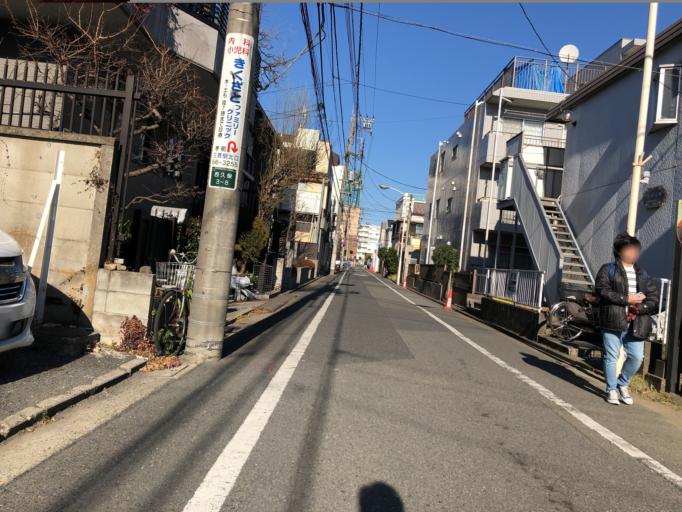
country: JP
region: Tokyo
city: Musashino
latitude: 35.7122
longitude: 139.5614
